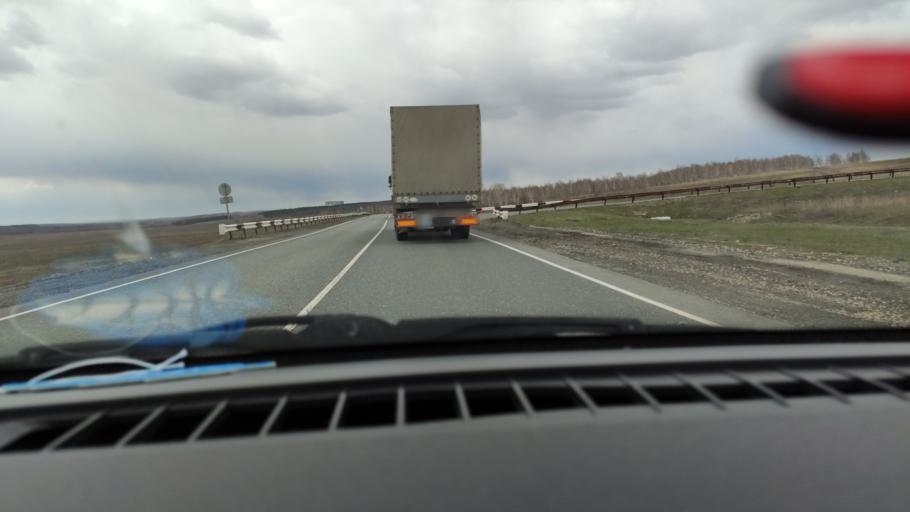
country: RU
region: Saratov
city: Sennoy
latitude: 52.1335
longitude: 46.8662
